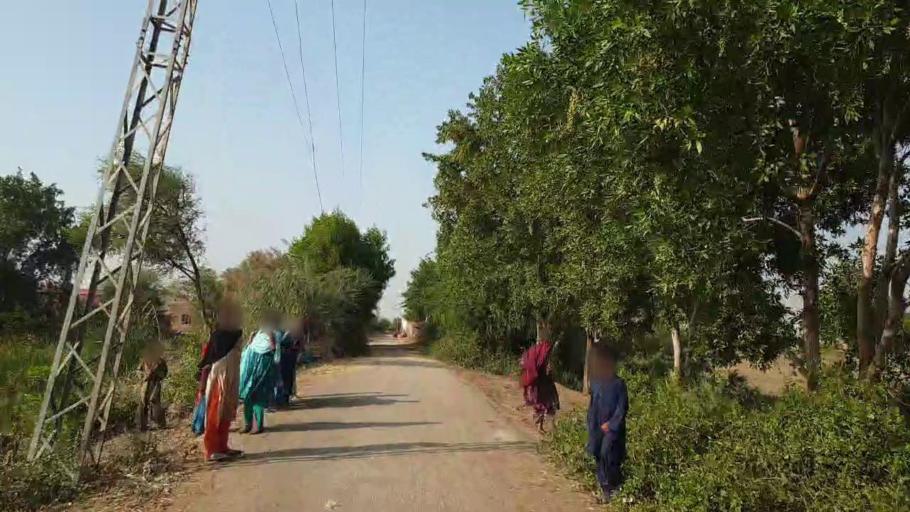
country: PK
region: Sindh
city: Bulri
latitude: 24.9926
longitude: 68.3726
